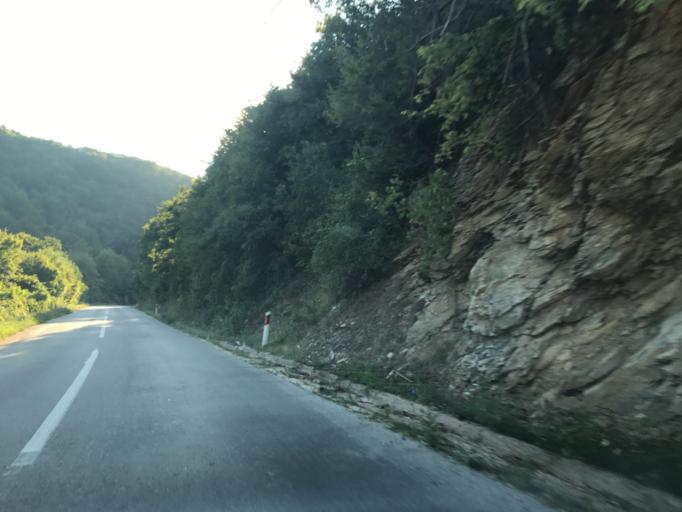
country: RO
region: Mehedinti
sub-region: Comuna Svinita
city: Svinita
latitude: 44.3255
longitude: 22.2067
